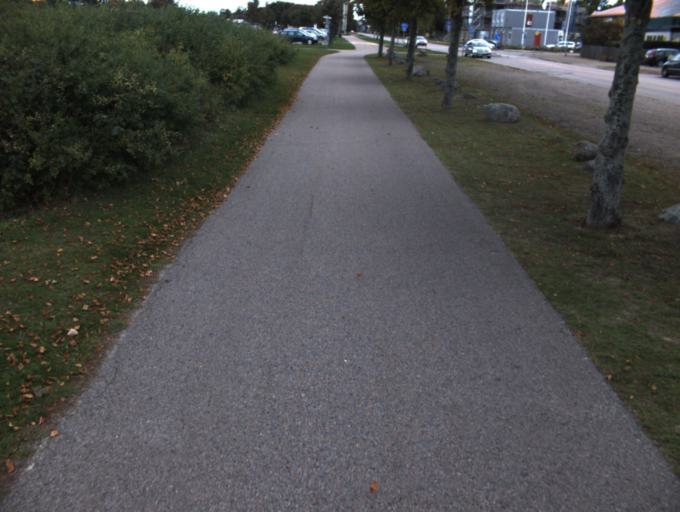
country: SE
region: Skane
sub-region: Helsingborg
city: Rydeback
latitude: 56.0020
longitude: 12.7321
